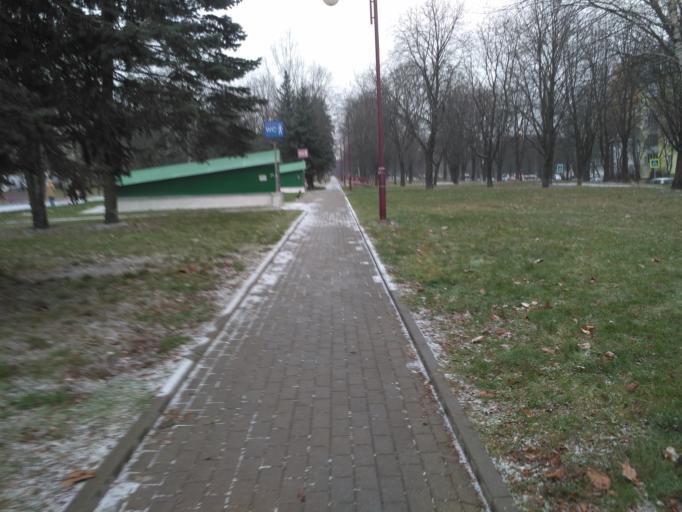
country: BY
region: Minsk
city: Novoye Medvezhino
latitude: 53.9100
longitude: 27.4883
